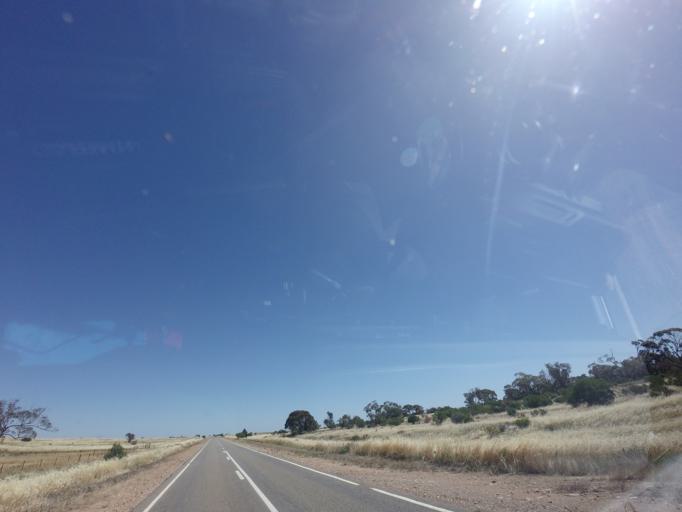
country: AU
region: South Australia
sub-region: Peterborough
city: Peterborough
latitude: -32.9232
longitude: 138.7703
